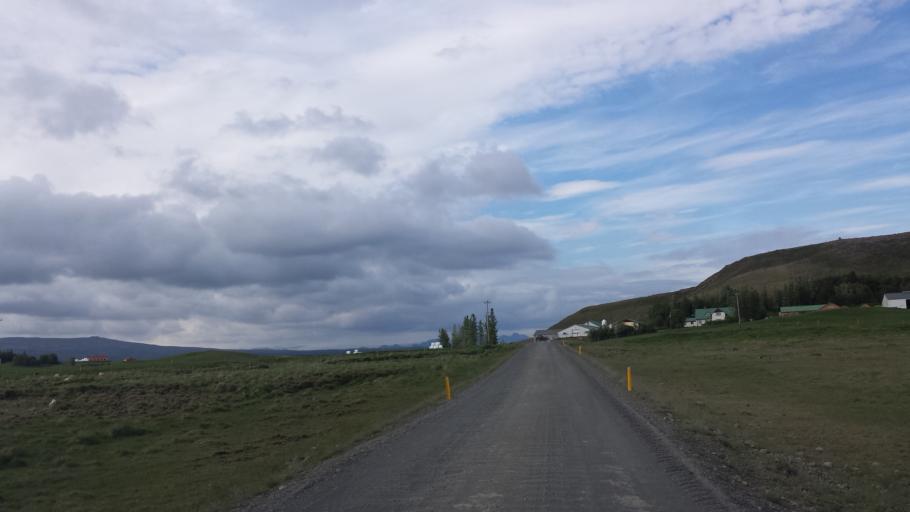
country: IS
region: South
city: Vestmannaeyjar
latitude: 64.2790
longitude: -20.2255
